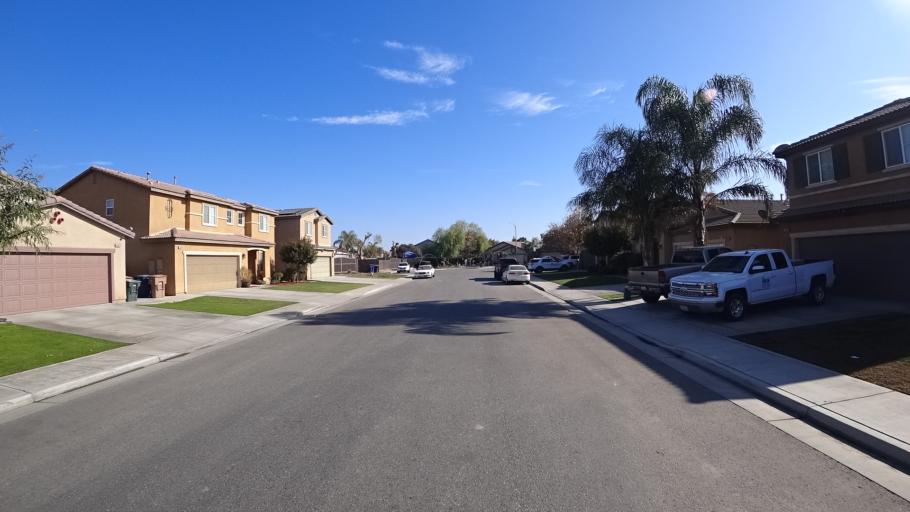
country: US
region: California
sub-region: Kern County
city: Greenfield
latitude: 35.2770
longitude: -119.0647
